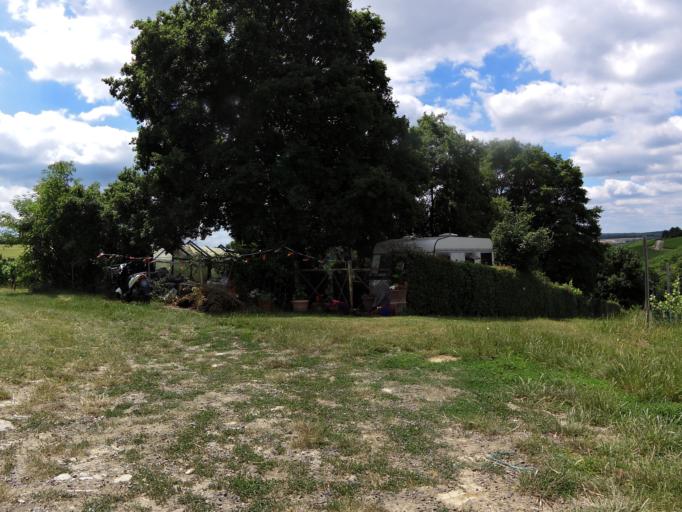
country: DE
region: Bavaria
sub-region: Regierungsbezirk Unterfranken
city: Randersacker
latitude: 49.7737
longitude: 9.9652
